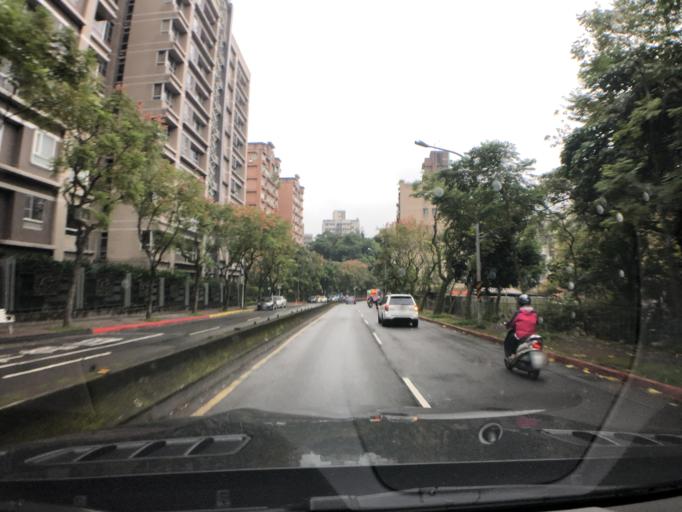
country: TW
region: Taipei
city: Taipei
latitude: 24.9902
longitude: 121.5523
